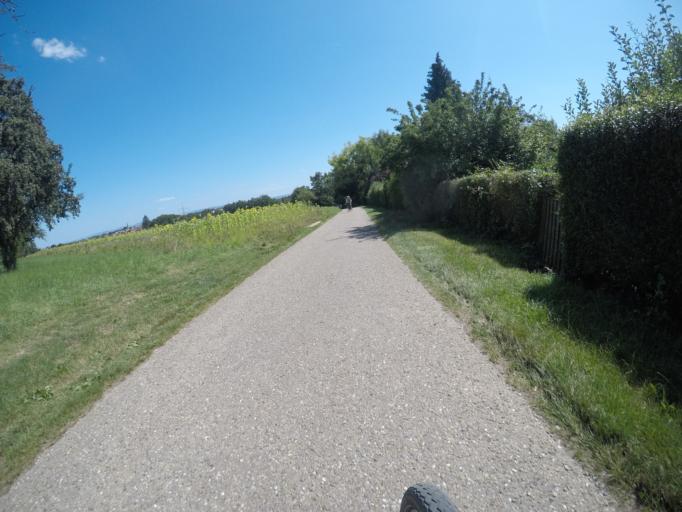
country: DE
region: Baden-Wuerttemberg
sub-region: Regierungsbezirk Stuttgart
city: Leinfelden-Echterdingen
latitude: 48.7062
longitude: 9.1932
